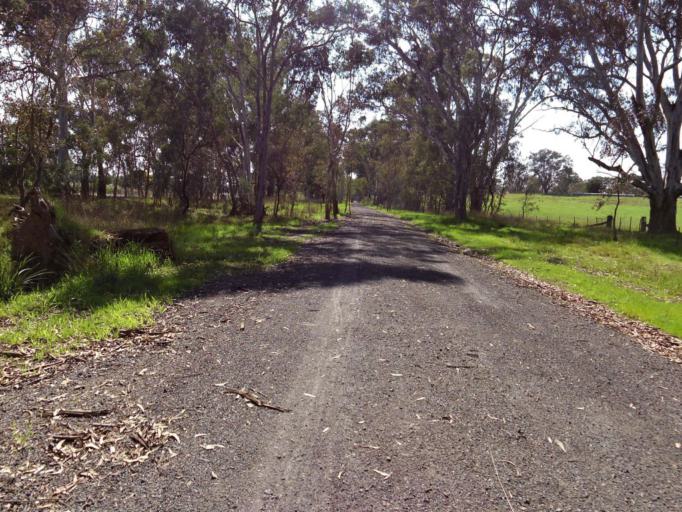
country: AU
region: Victoria
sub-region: Murrindindi
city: Alexandra
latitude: -37.1190
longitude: 145.6037
